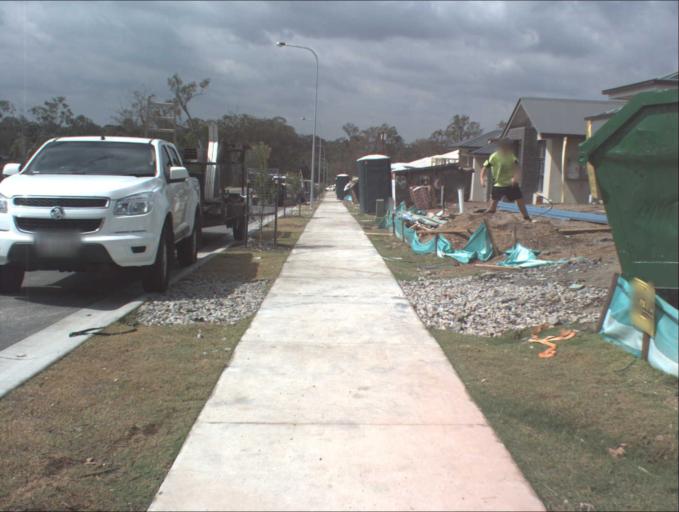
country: AU
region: Queensland
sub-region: Logan
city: Woodridge
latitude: -27.6632
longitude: 153.0832
